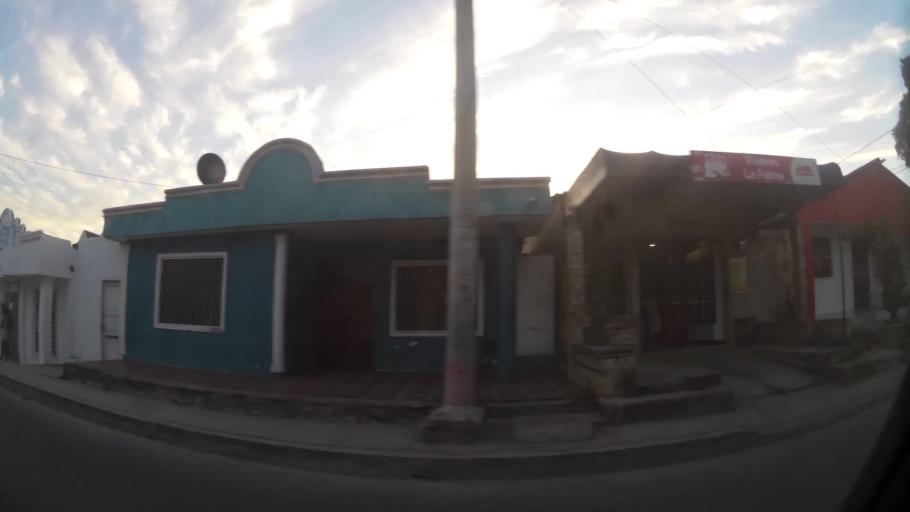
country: CO
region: Atlantico
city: Barranquilla
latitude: 10.9619
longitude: -74.8276
